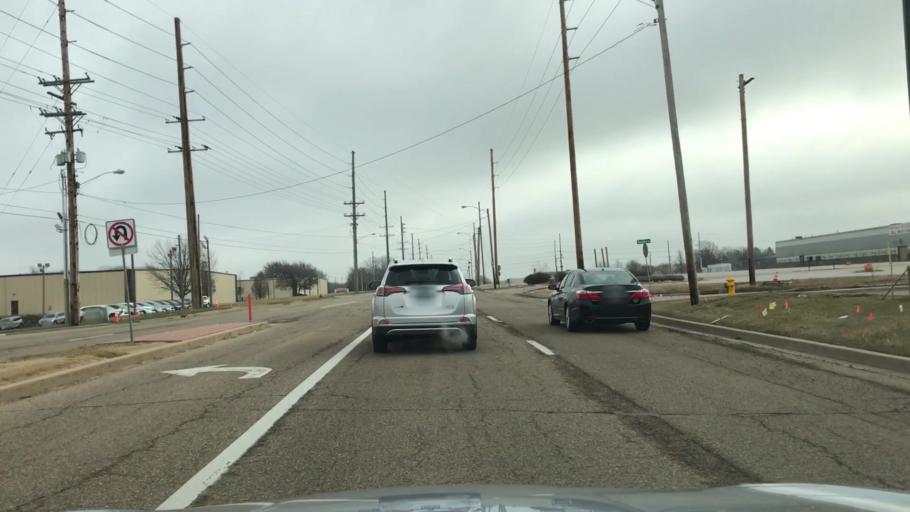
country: US
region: Illinois
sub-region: McLean County
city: Normal
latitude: 40.5026
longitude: -88.9518
